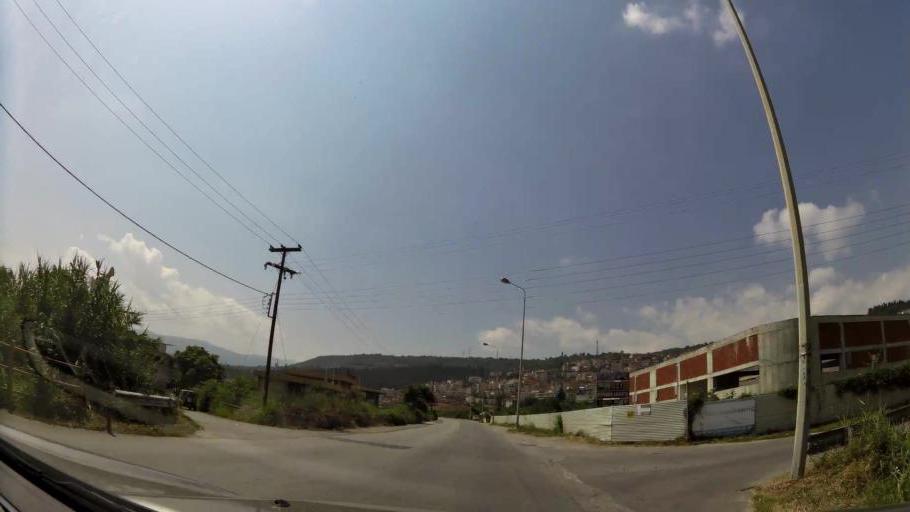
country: GR
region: Central Macedonia
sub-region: Nomos Imathias
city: Veroia
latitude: 40.5177
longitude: 22.2123
